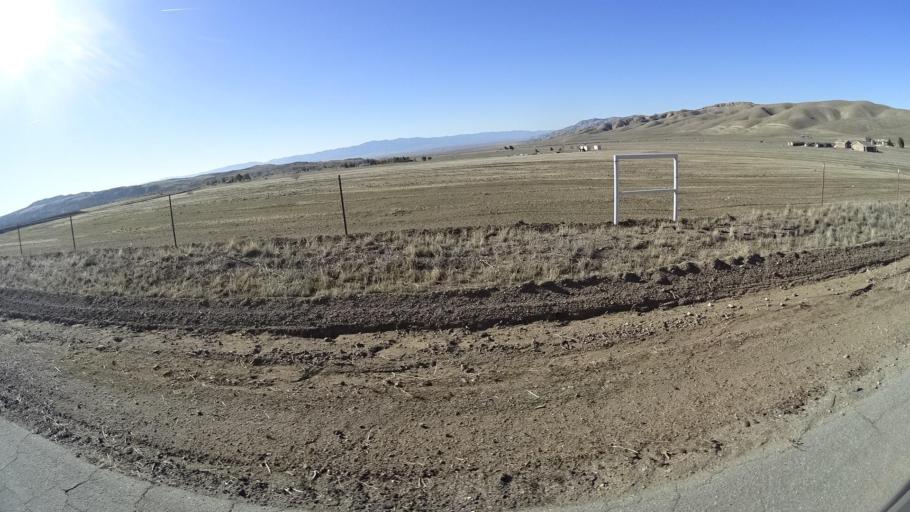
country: US
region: California
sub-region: Kern County
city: Maricopa
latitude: 34.9394
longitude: -119.4540
